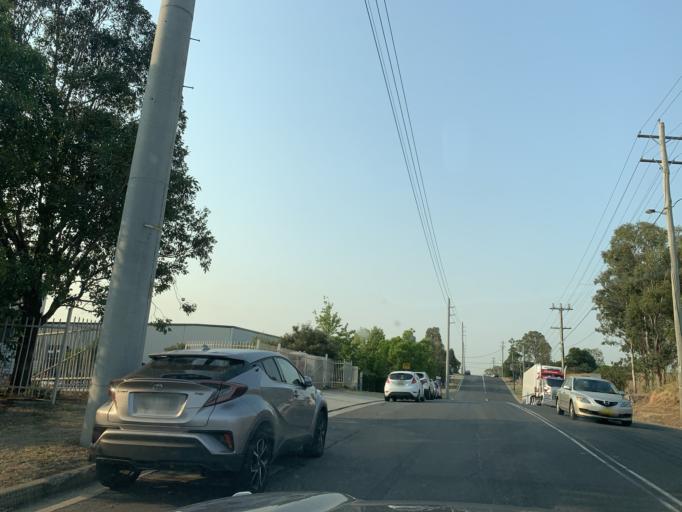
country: AU
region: New South Wales
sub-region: Fairfield
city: Horsley Park
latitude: -33.8378
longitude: 150.8813
